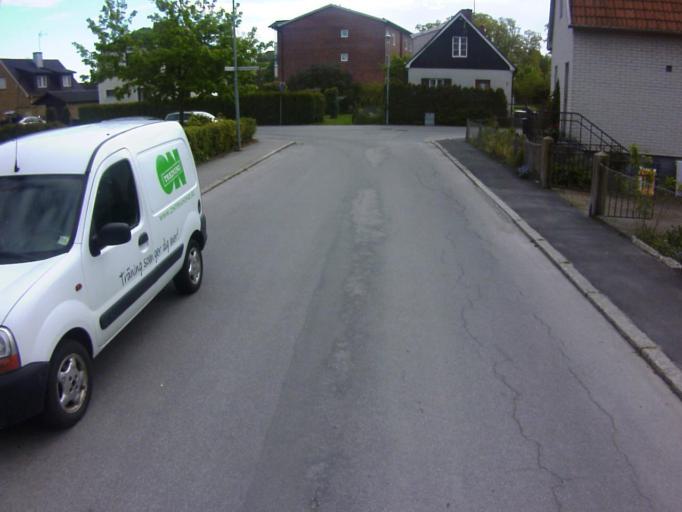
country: SE
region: Blekinge
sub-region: Solvesborgs Kommun
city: Soelvesborg
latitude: 56.0560
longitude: 14.5863
